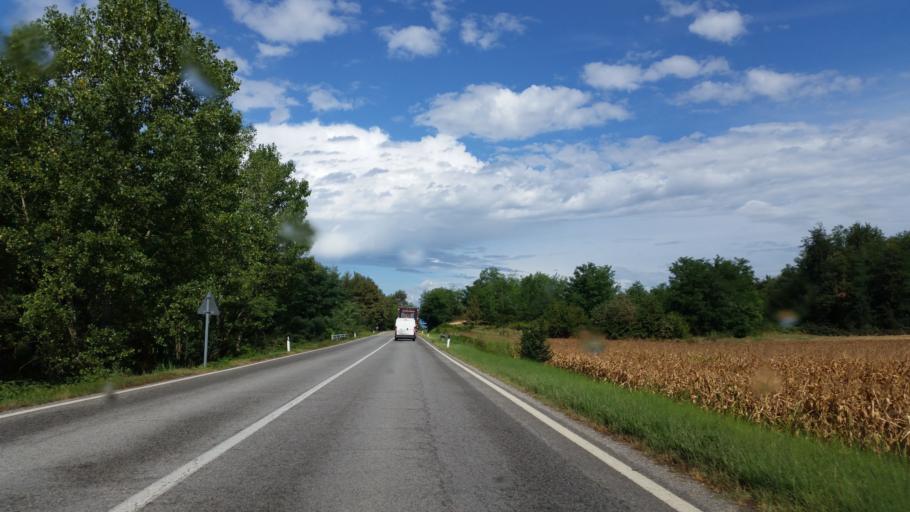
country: IT
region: Piedmont
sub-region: Provincia di Cuneo
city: Monta
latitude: 44.8298
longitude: 7.9290
